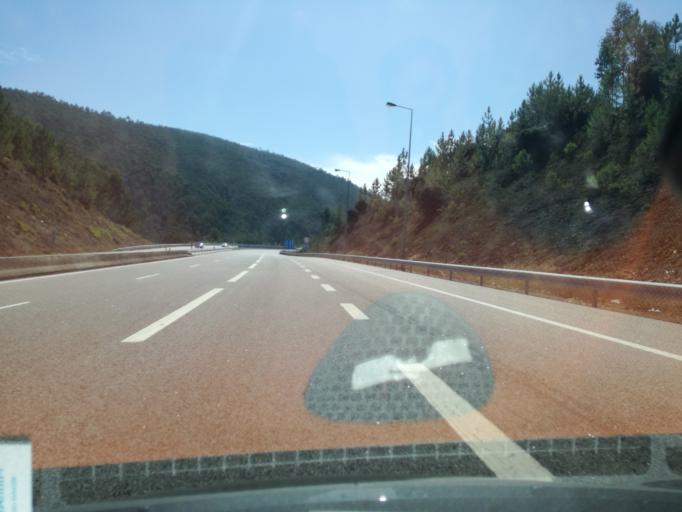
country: ES
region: Galicia
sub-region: Provincia de Pontevedra
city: O Rosal
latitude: 41.8761
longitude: -8.7867
